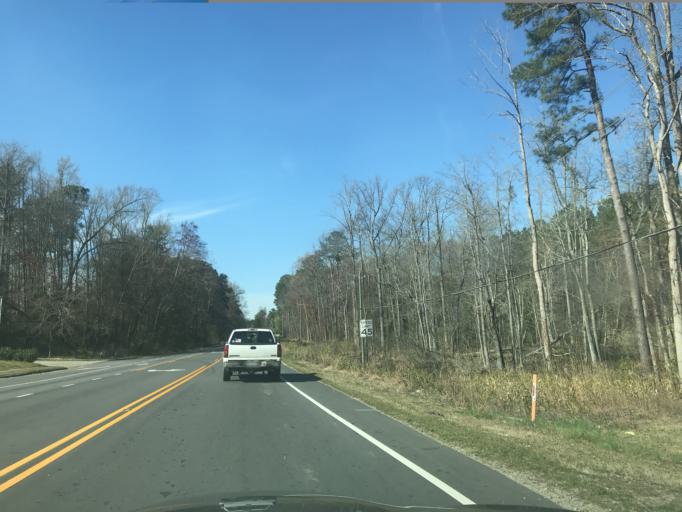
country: US
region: North Carolina
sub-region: Wake County
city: Fuquay-Varina
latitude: 35.5832
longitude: -78.7568
